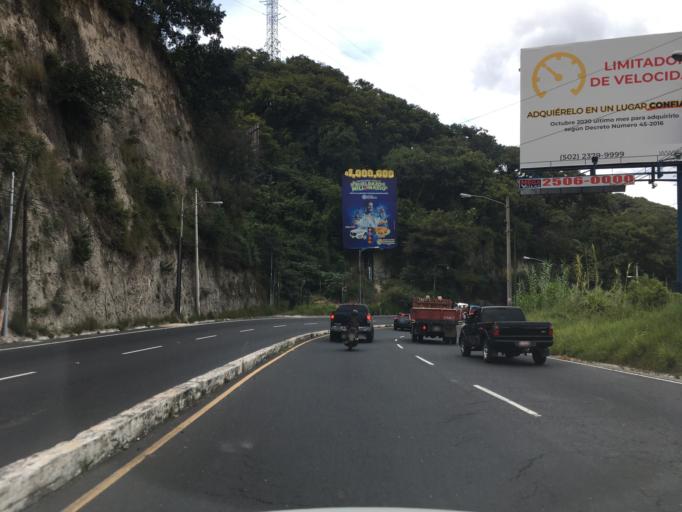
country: GT
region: Guatemala
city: Mixco
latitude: 14.5910
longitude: -90.5746
